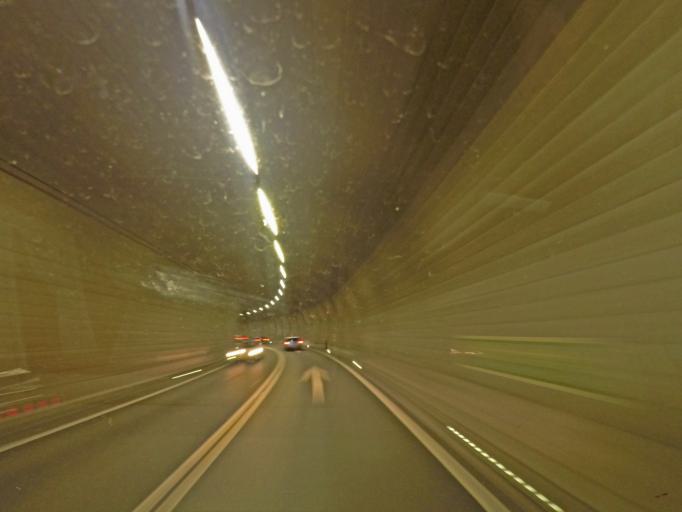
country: CH
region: Uri
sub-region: Uri
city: Flueelen
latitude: 46.9316
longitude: 8.6143
